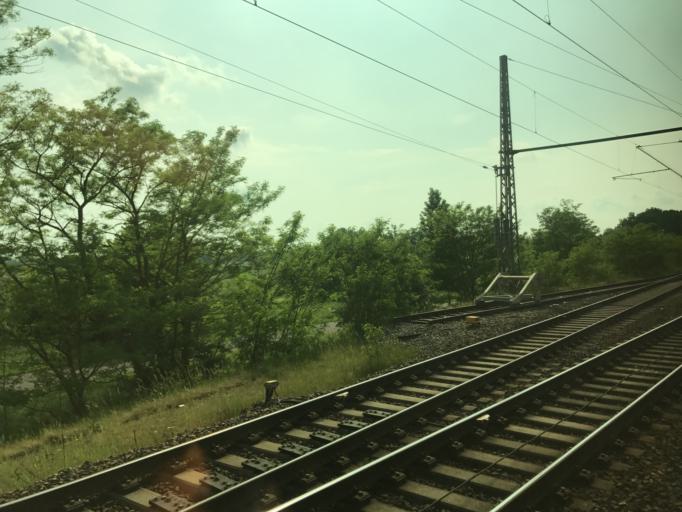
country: DE
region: Brandenburg
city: Nennhausen
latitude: 52.5992
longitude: 12.5163
